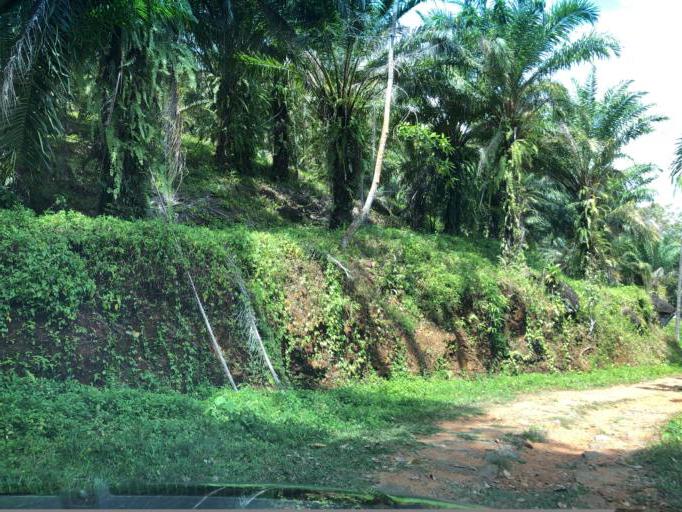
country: LK
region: Western
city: Horawala Junction
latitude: 6.5494
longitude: 80.0885
